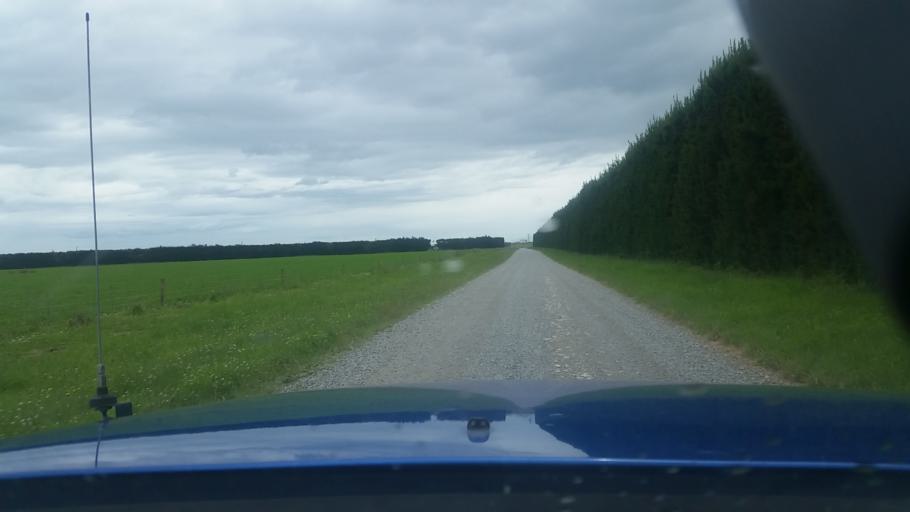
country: NZ
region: Canterbury
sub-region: Ashburton District
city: Rakaia
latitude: -43.9045
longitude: 172.0598
